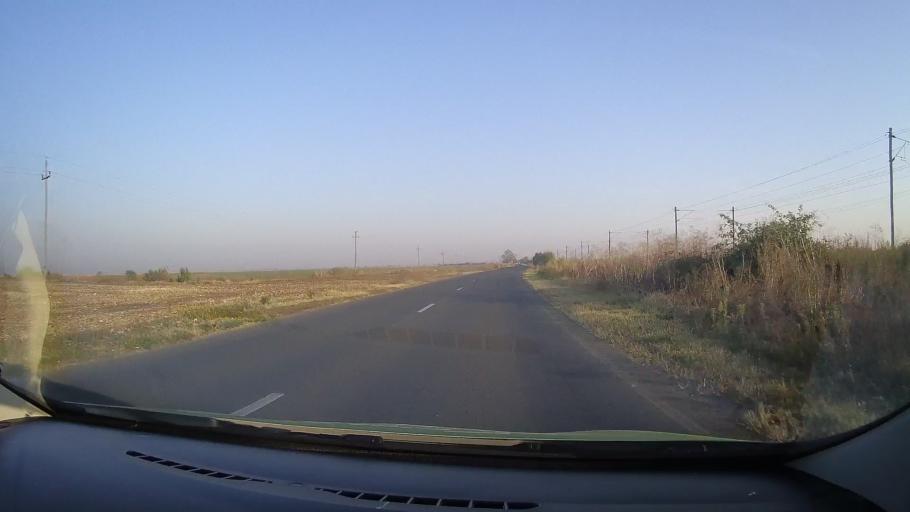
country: RO
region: Arad
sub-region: Comuna Sofronea
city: Sofronea
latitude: 46.2947
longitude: 21.3111
